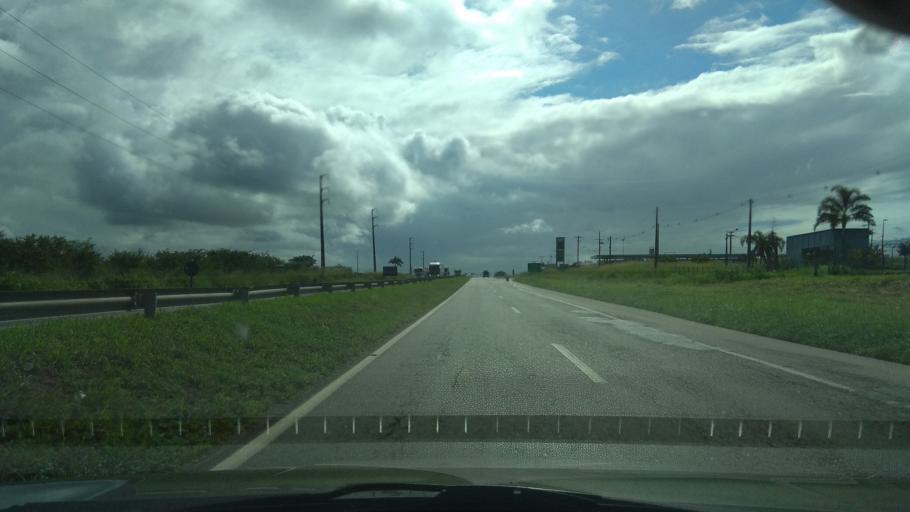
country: BR
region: Bahia
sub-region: Conceicao Do Jacuipe
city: Conceicao do Jacuipe
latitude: -12.3418
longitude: -38.8435
